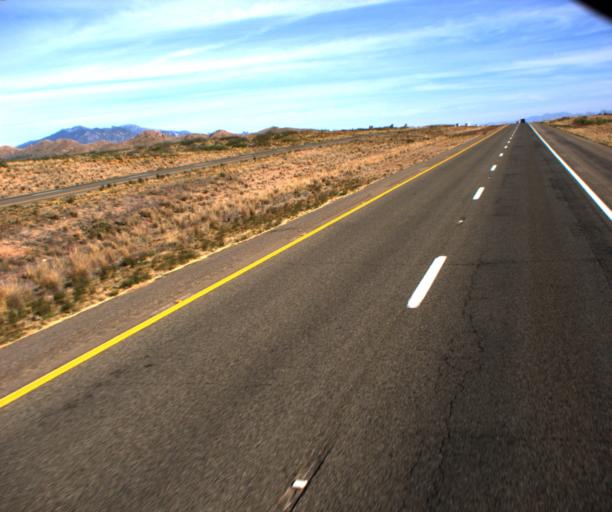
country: US
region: Arizona
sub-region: Graham County
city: Swift Trail Junction
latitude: 32.4826
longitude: -109.6730
